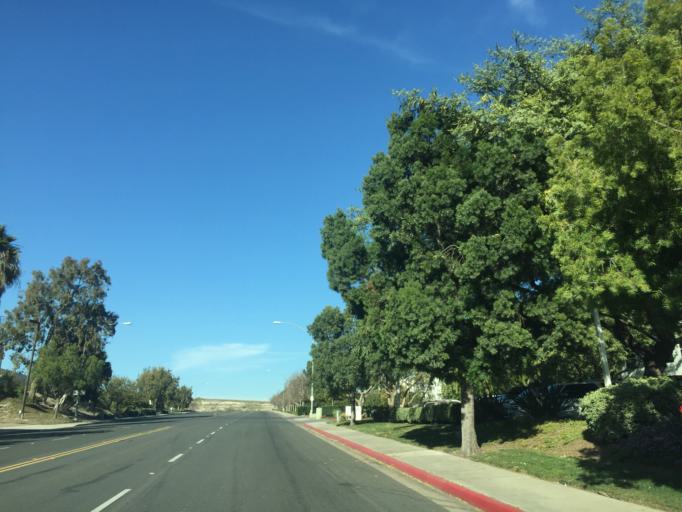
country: MX
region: Baja California
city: Tijuana
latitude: 32.5579
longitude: -116.9320
